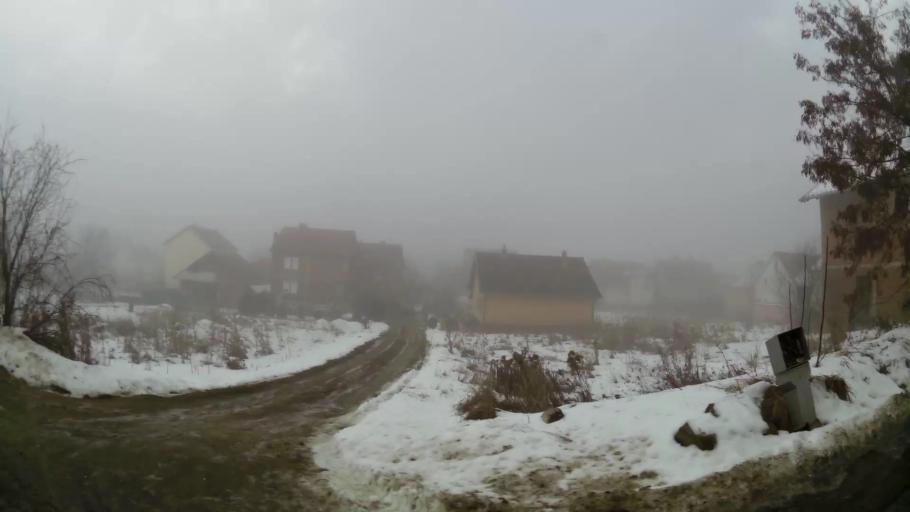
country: XK
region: Pristina
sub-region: Komuna e Prishtines
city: Pristina
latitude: 42.6414
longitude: 21.1488
